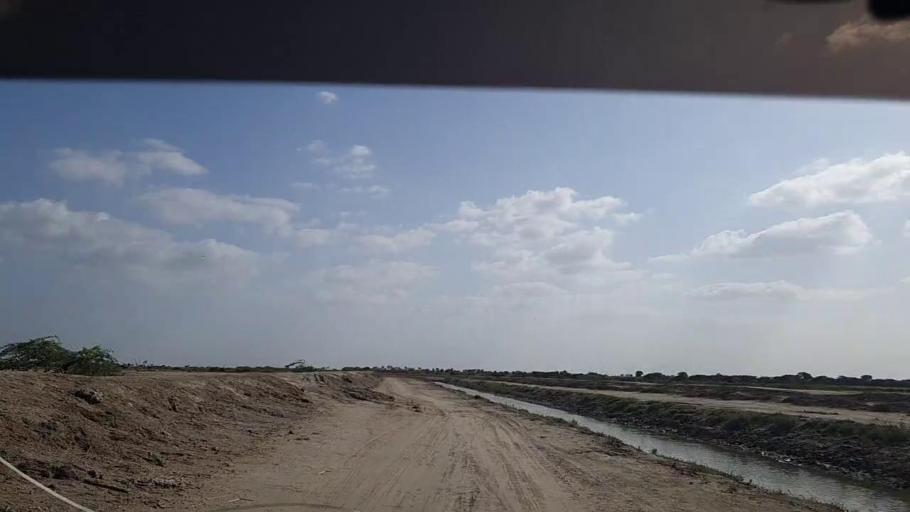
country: PK
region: Sindh
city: Kadhan
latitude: 24.4548
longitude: 68.8583
